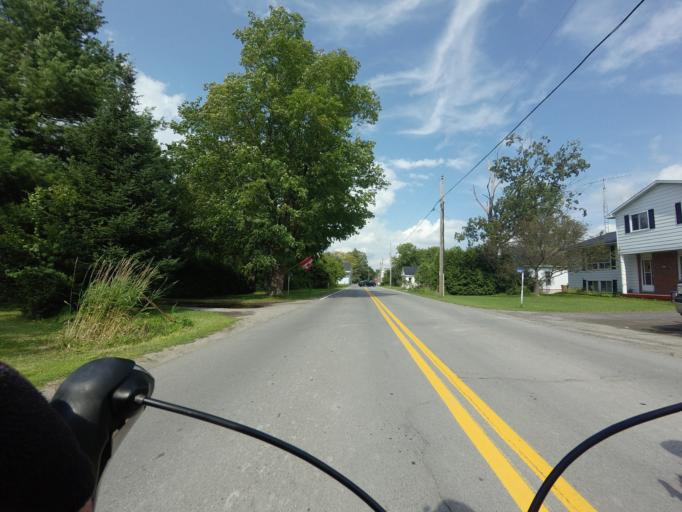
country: CA
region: Ontario
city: Brockville
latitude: 44.7605
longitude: -75.7400
